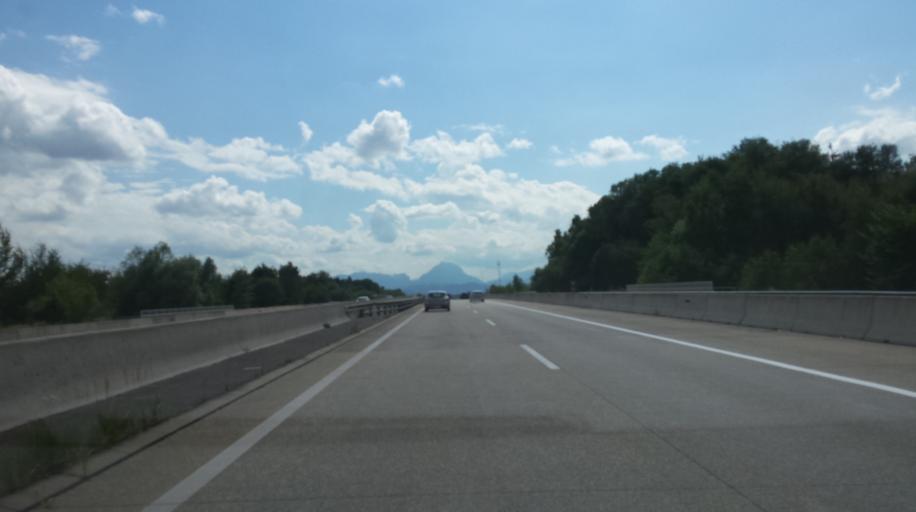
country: AT
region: Upper Austria
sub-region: Wels-Land
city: Sattledt
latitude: 48.0648
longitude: 14.0400
